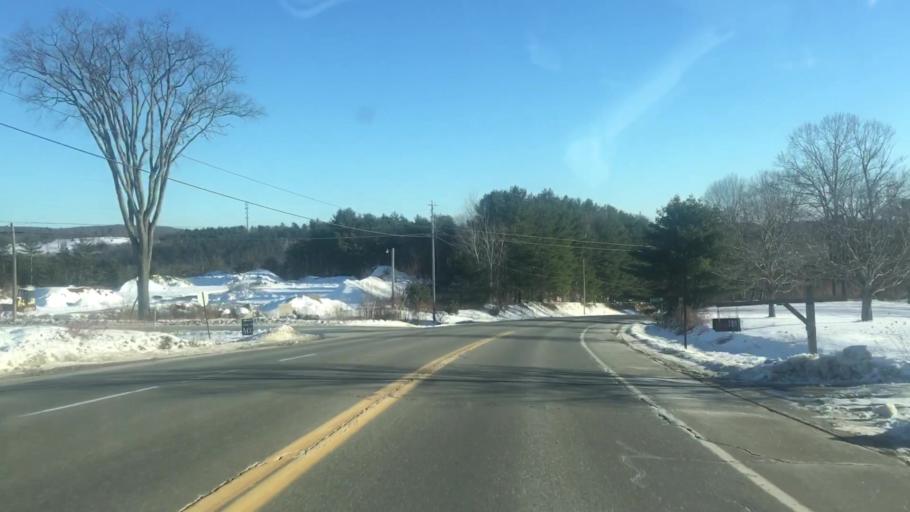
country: US
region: Maine
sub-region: Somerset County
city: Norridgewock
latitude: 44.7219
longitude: -69.7996
